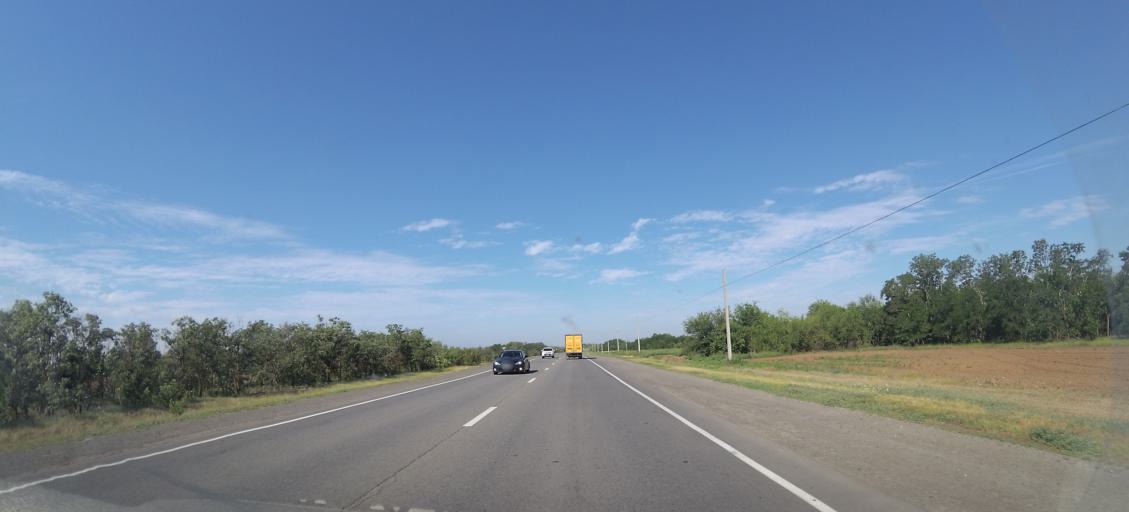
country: RU
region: Volgograd
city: Oktyabr'skiy
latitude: 48.6919
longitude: 43.7799
